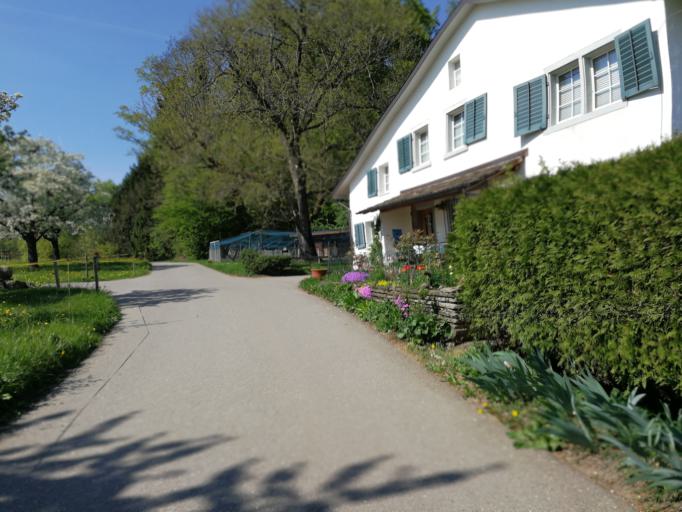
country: CH
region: Zurich
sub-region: Bezirk Meilen
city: Hombrechtikon
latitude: 47.2574
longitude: 8.7609
